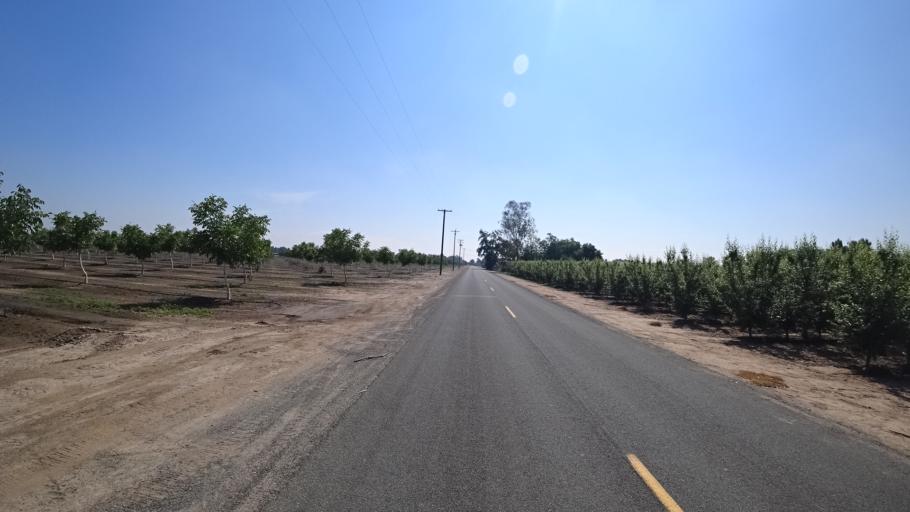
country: US
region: California
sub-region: Fresno County
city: Kingsburg
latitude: 36.4524
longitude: -119.5570
